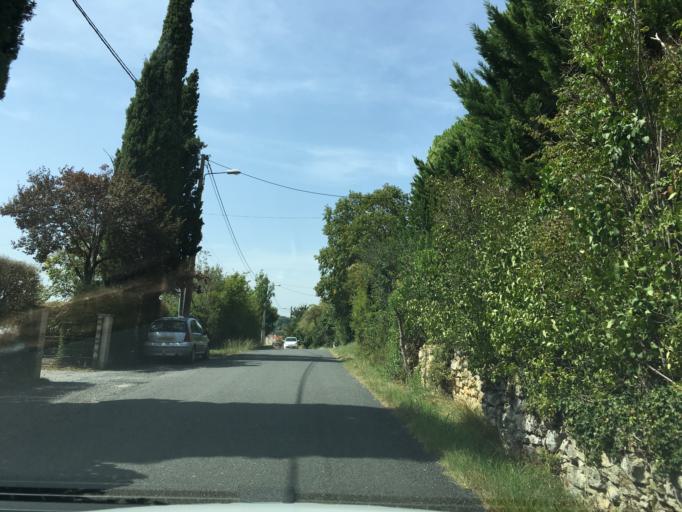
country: FR
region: Midi-Pyrenees
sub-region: Departement du Tarn
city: Castres
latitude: 43.6269
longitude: 2.2369
